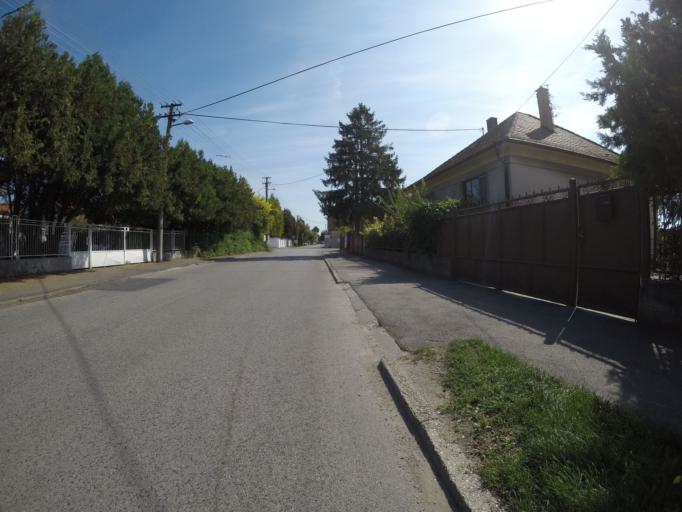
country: SK
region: Trnavsky
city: Dunajska Streda
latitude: 47.9872
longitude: 17.6109
